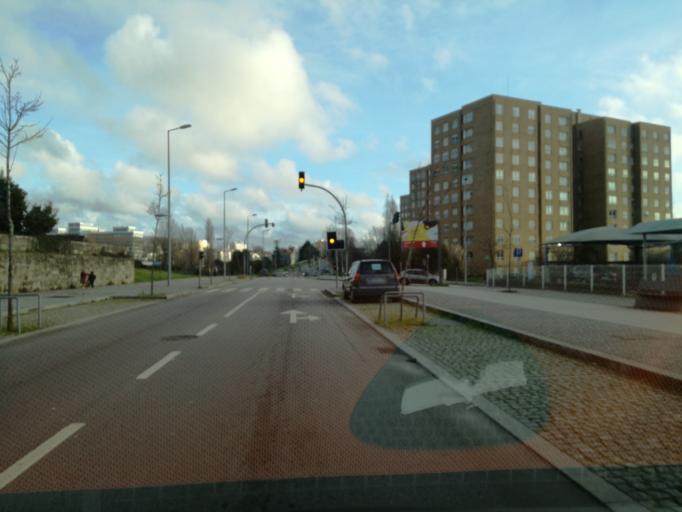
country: PT
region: Porto
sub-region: Matosinhos
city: Senhora da Hora
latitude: 41.1749
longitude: -8.6344
